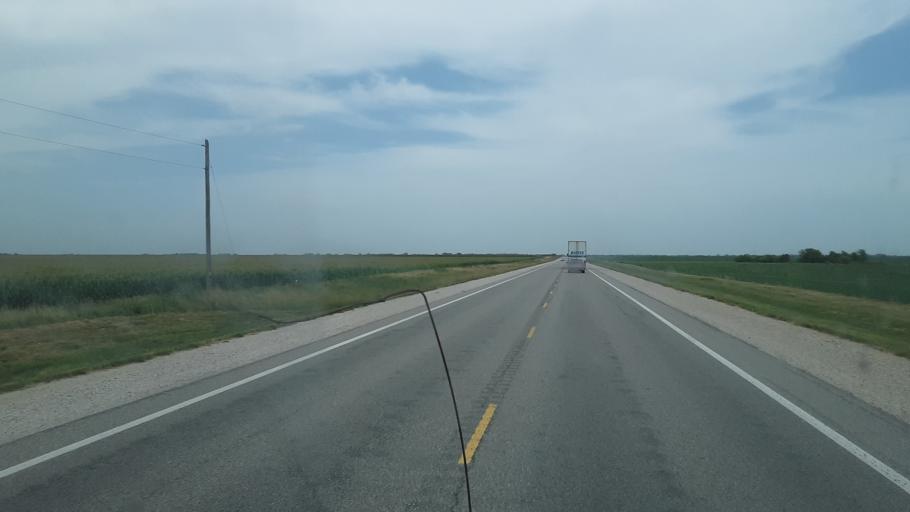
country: US
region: Kansas
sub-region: Allen County
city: Iola
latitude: 37.9216
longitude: -95.2437
